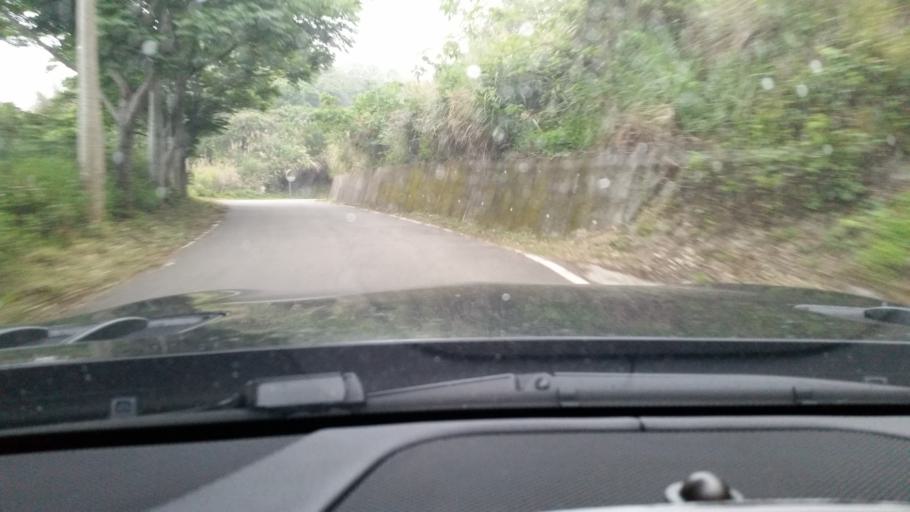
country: TW
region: Taiwan
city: Fengyuan
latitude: 24.3456
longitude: 120.7779
